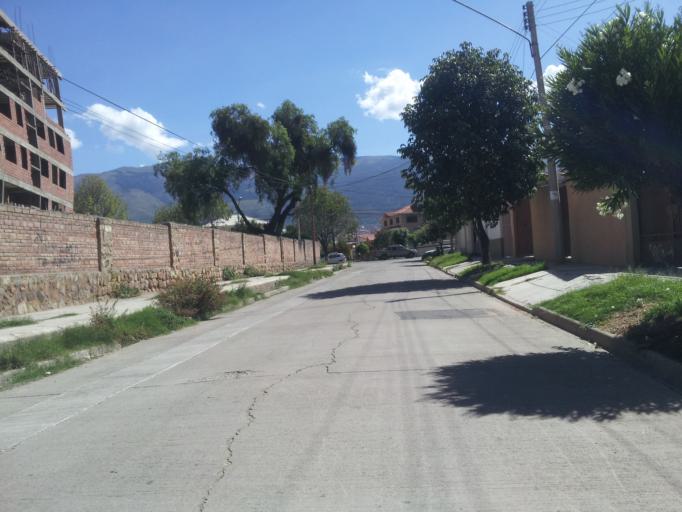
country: BO
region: Cochabamba
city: Cochabamba
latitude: -17.3840
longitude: -66.1710
